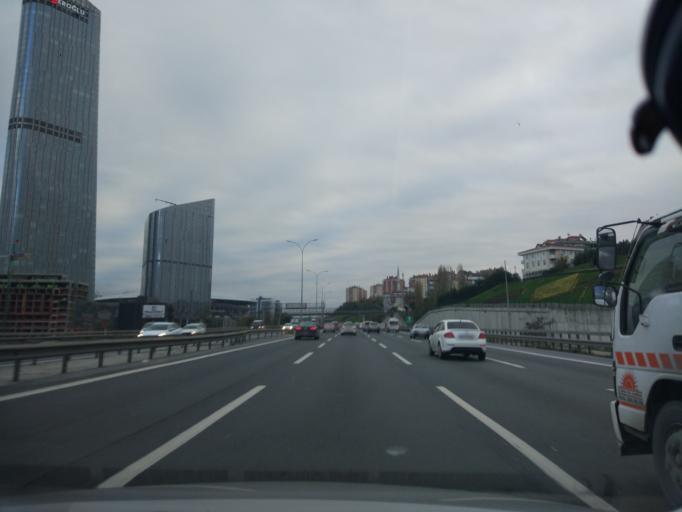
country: TR
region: Istanbul
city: Sisli
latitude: 41.1003
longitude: 28.9814
